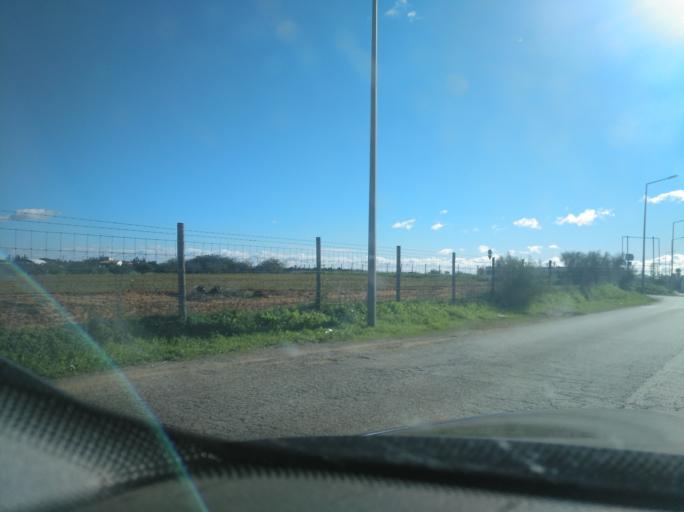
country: PT
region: Faro
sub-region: Vila Real de Santo Antonio
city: Monte Gordo
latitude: 37.1740
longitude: -7.5195
